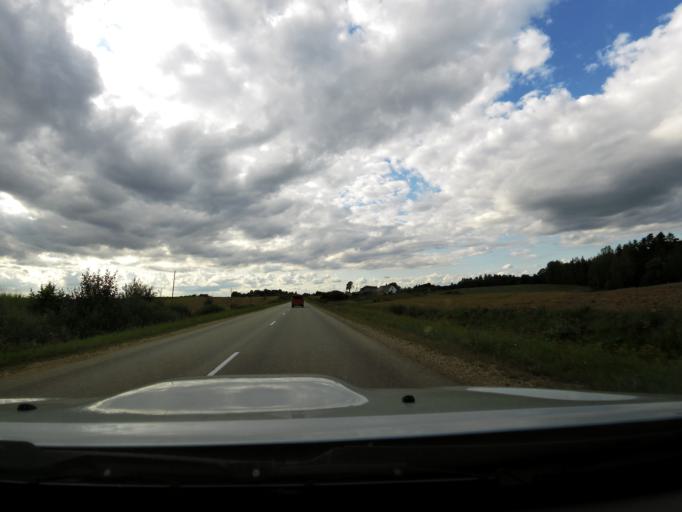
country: LV
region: Ilukste
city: Ilukste
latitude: 55.9726
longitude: 26.0248
